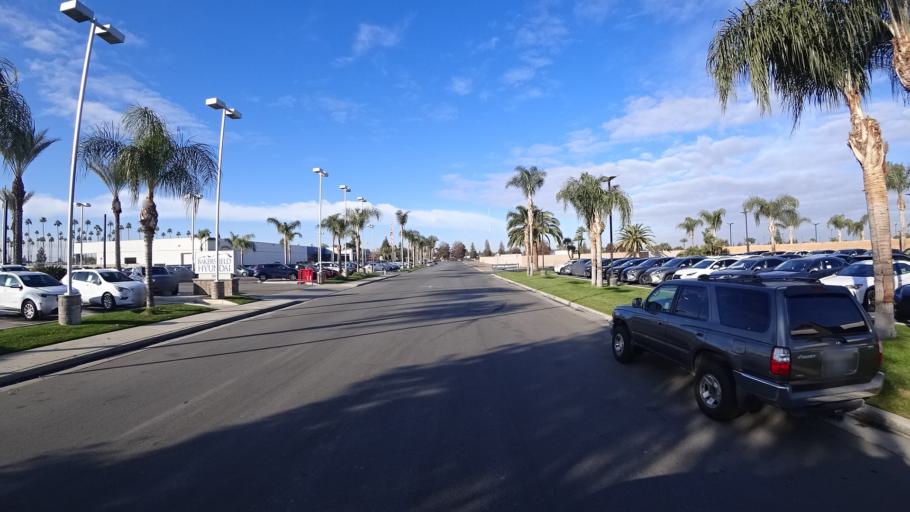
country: US
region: California
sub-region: Kern County
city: Greenfield
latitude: 35.3072
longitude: -119.0367
